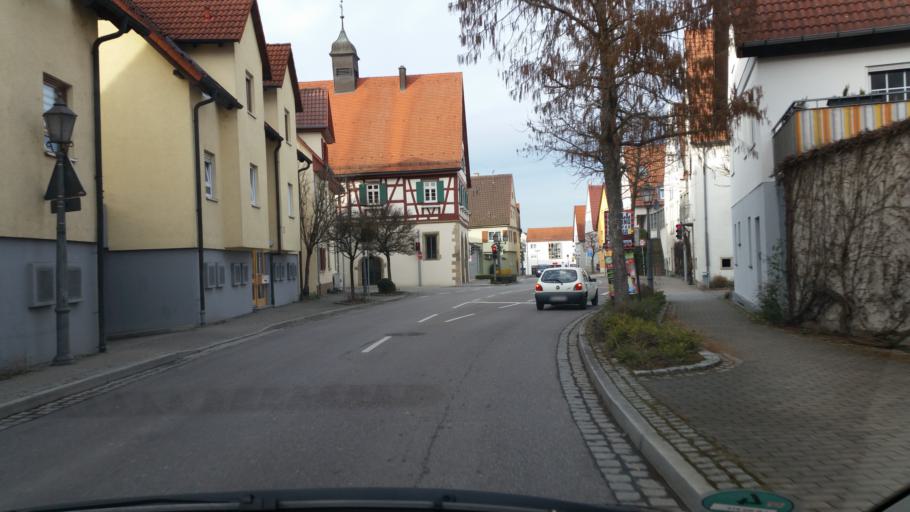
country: DE
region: Baden-Wuerttemberg
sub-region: Regierungsbezirk Stuttgart
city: Pleidelsheim
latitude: 48.9586
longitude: 9.2050
